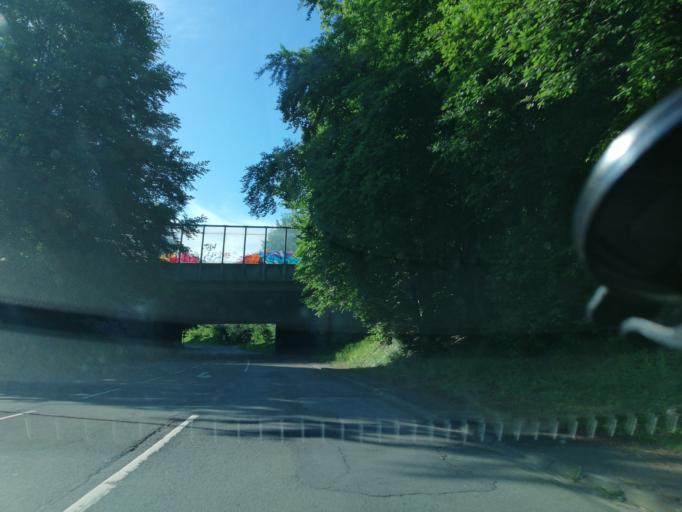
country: DE
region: North Rhine-Westphalia
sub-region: Regierungsbezirk Arnsberg
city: Schwelm
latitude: 51.3223
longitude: 7.2886
